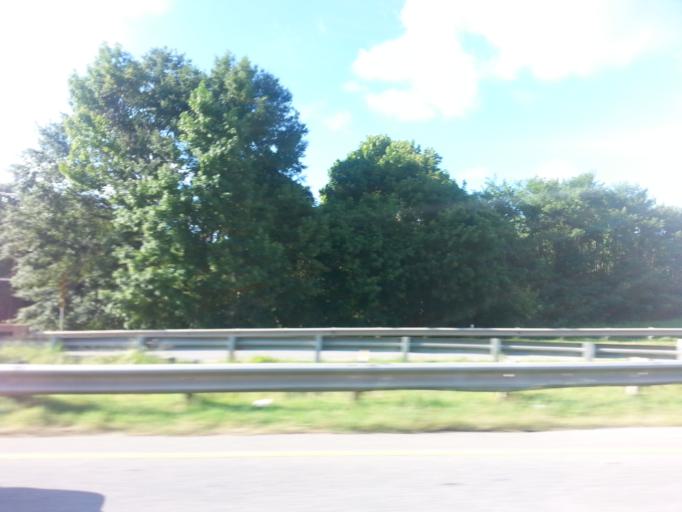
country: US
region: Alabama
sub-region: Colbert County
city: Tuscumbia
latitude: 34.7117
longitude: -87.7228
